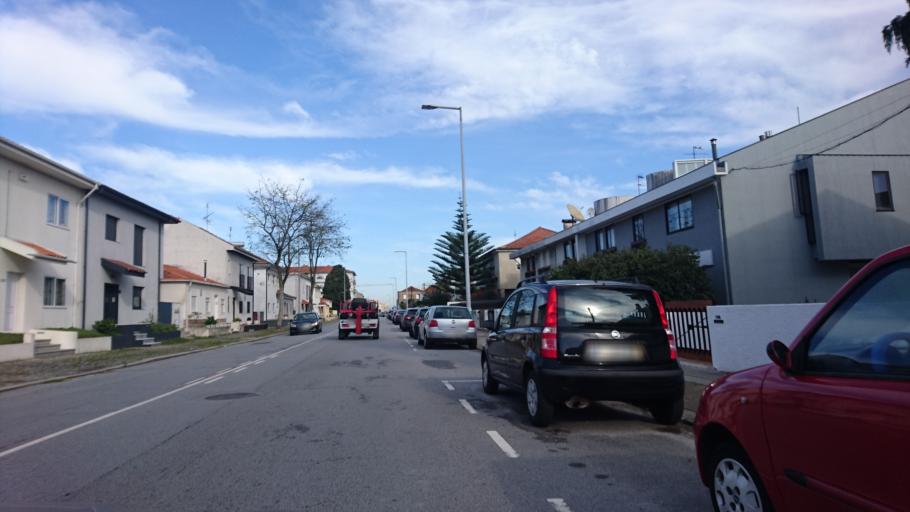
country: PT
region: Porto
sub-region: Matosinhos
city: Sao Mamede de Infesta
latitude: 41.1797
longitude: -8.6092
